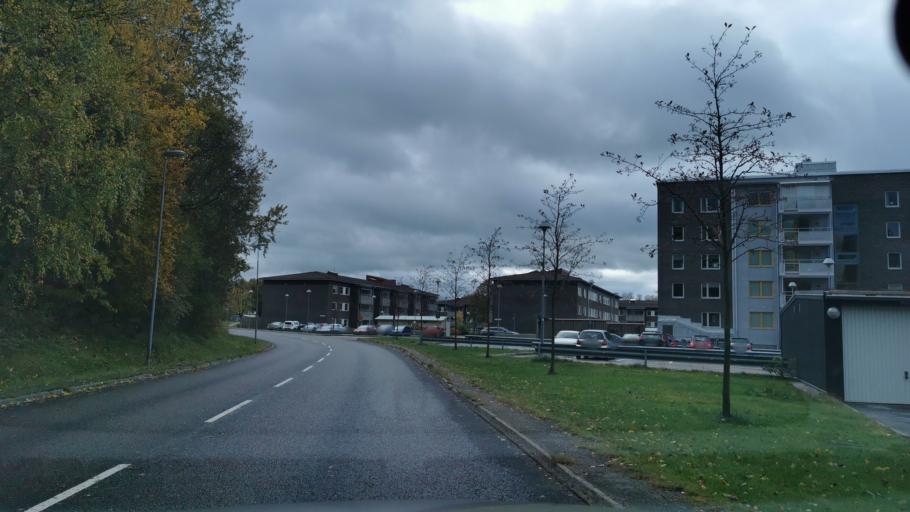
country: SE
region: Vaestra Goetaland
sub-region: Partille Kommun
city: Partille
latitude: 57.7182
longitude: 12.0806
